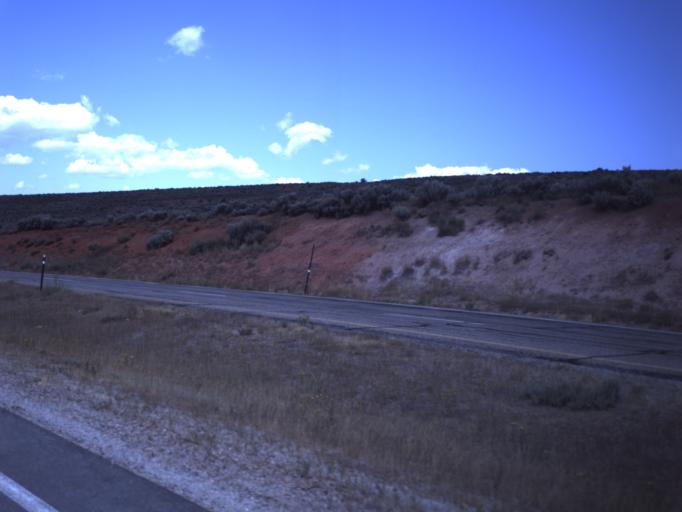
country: US
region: Utah
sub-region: Rich County
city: Randolph
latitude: 41.8079
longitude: -111.2509
